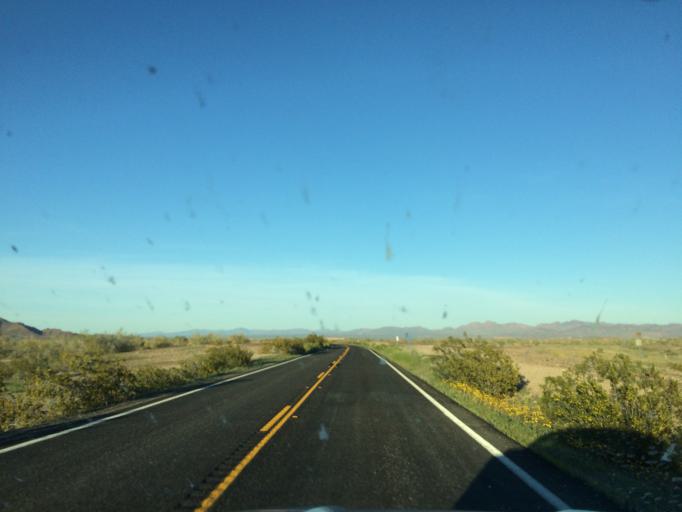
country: US
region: California
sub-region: Riverside County
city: Mesa Verde
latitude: 33.2474
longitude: -114.8213
